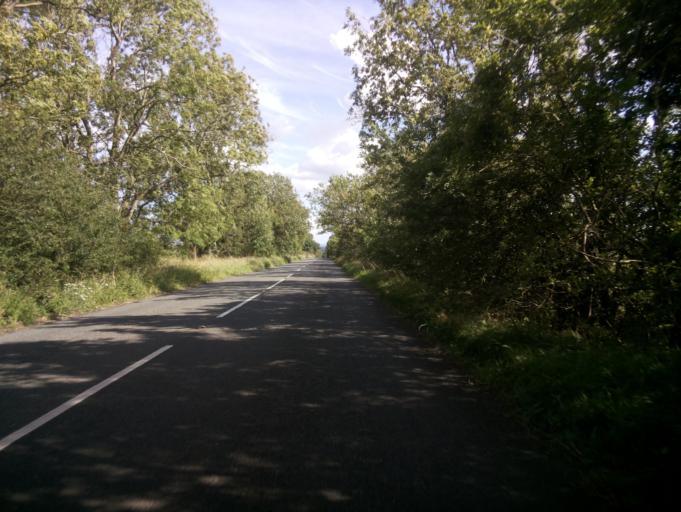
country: GB
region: England
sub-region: Gloucestershire
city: Cirencester
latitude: 51.7431
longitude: -1.9933
